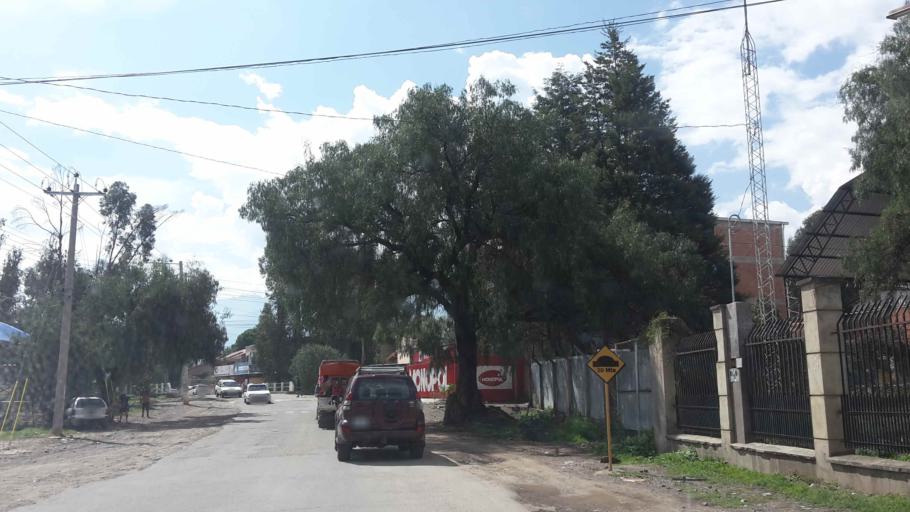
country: BO
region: Cochabamba
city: Cochabamba
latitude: -17.3364
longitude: -66.2290
